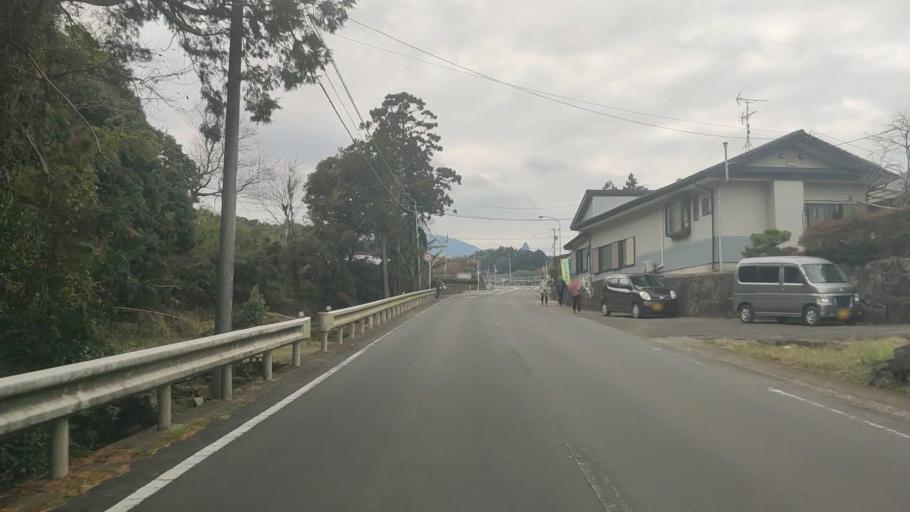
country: JP
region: Nagasaki
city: Shimabara
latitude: 32.8357
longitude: 130.2926
